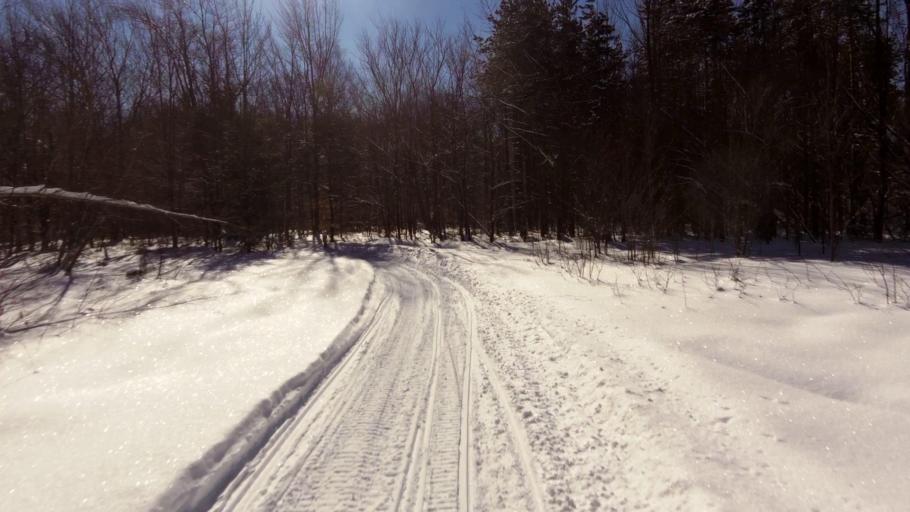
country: US
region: New York
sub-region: Chautauqua County
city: Fredonia
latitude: 42.3503
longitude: -79.1874
